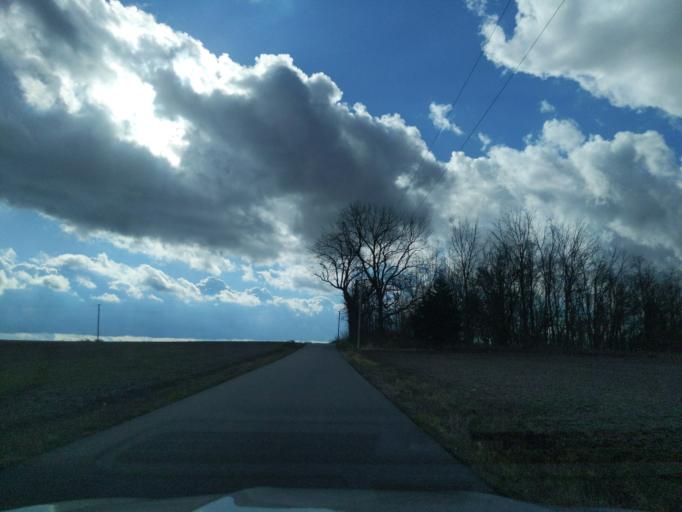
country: US
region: Indiana
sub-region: Decatur County
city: Greensburg
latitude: 39.3816
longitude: -85.5082
